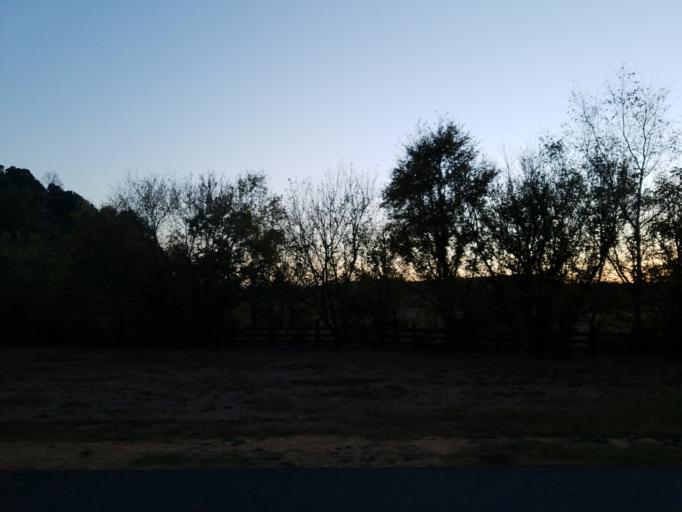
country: US
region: Georgia
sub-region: Gordon County
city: Calhoun
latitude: 34.5879
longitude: -84.9578
